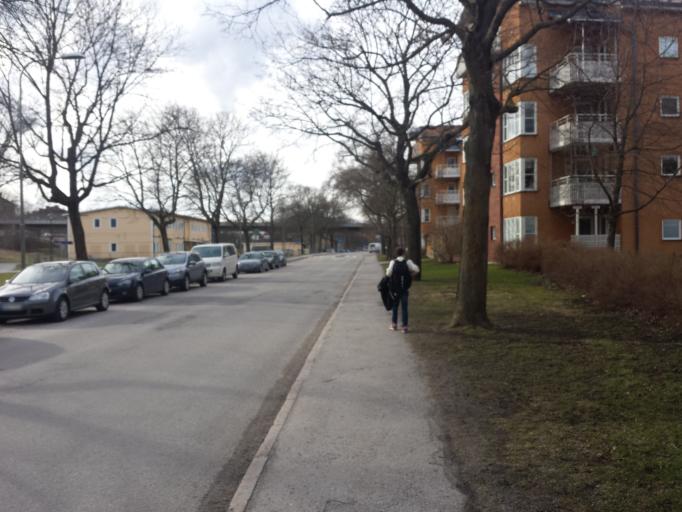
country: SE
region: Stockholm
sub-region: Nacka Kommun
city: Nacka
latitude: 59.2879
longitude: 18.1179
